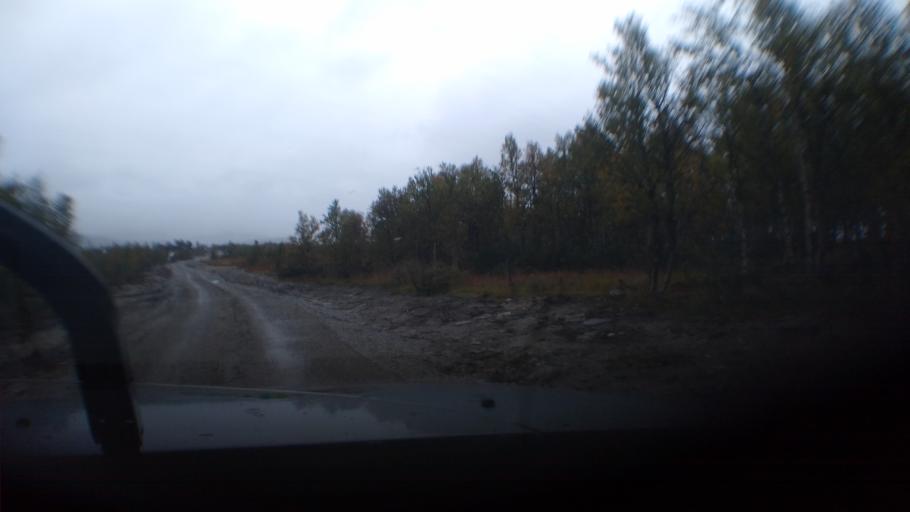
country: NO
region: Oppland
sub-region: Ringebu
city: Ringebu
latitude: 61.6571
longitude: 10.1038
